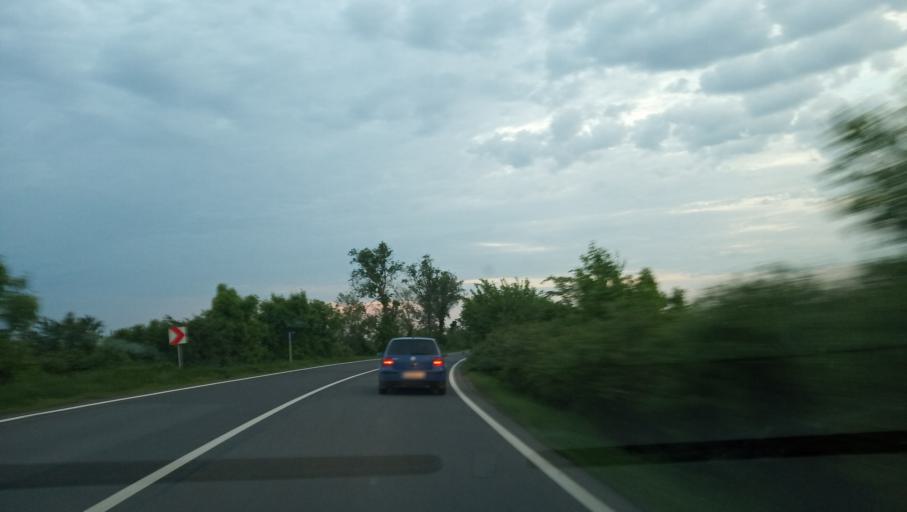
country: RO
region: Timis
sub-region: Comuna Padureni
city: Padureni
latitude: 45.6205
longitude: 21.1925
